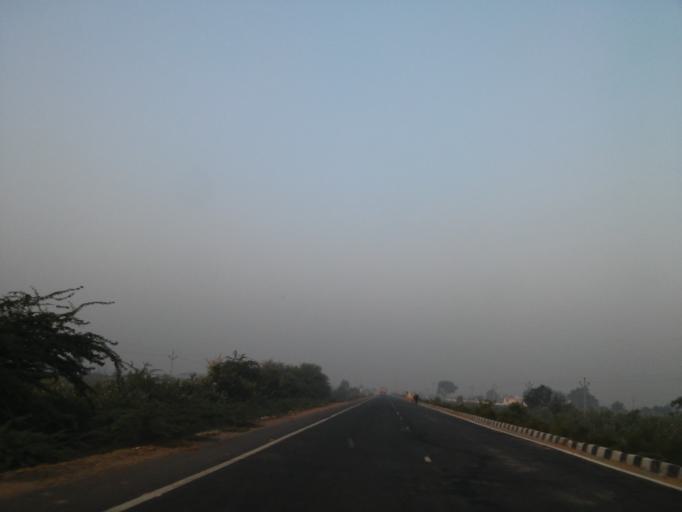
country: IN
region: Gujarat
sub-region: Surendranagar
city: Halvad
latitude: 23.0181
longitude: 71.0089
